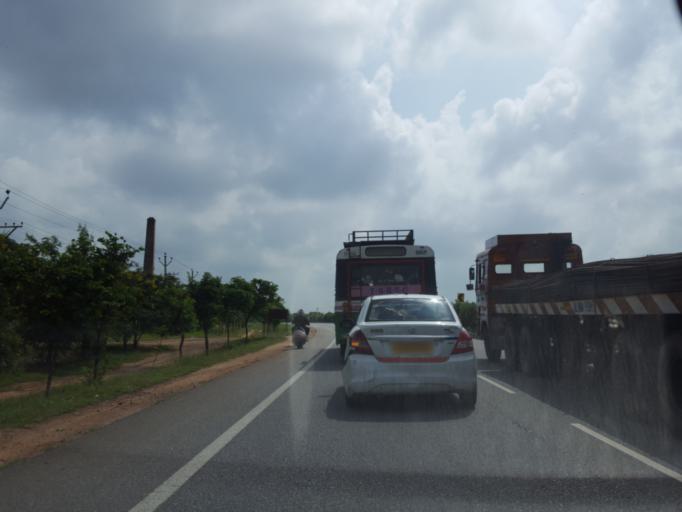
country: IN
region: Telangana
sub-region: Nalgonda
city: Bhongir
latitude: 17.2299
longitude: 78.9941
